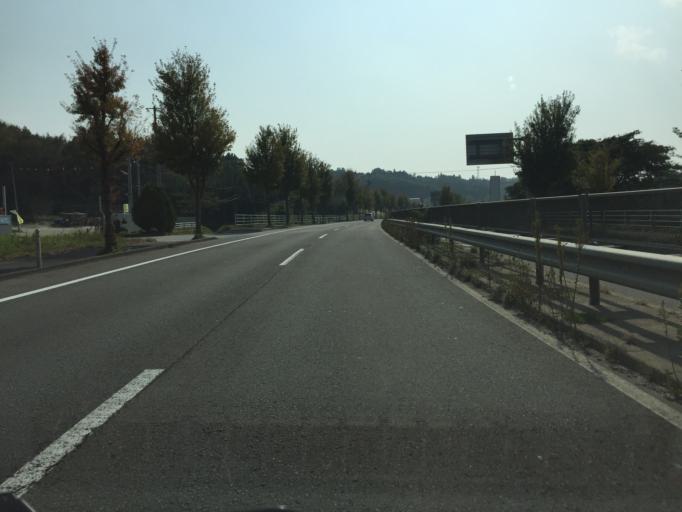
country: JP
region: Fukushima
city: Nihommatsu
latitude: 37.6281
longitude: 140.4812
